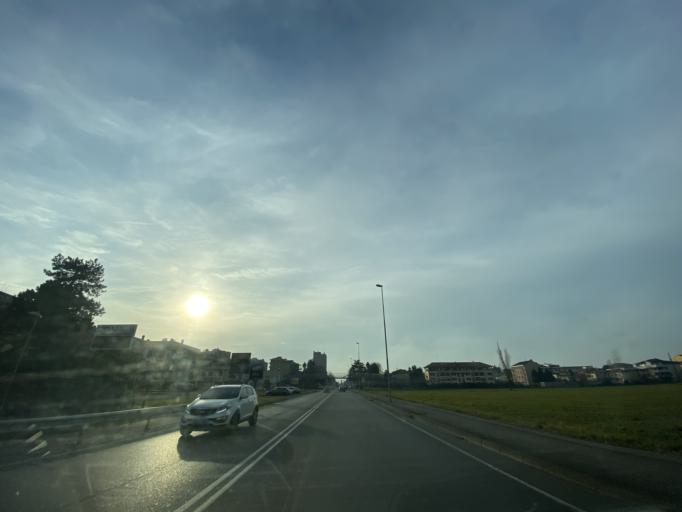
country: IT
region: Lombardy
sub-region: Citta metropolitana di Milano
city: Pioltello
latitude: 45.5153
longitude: 9.3356
